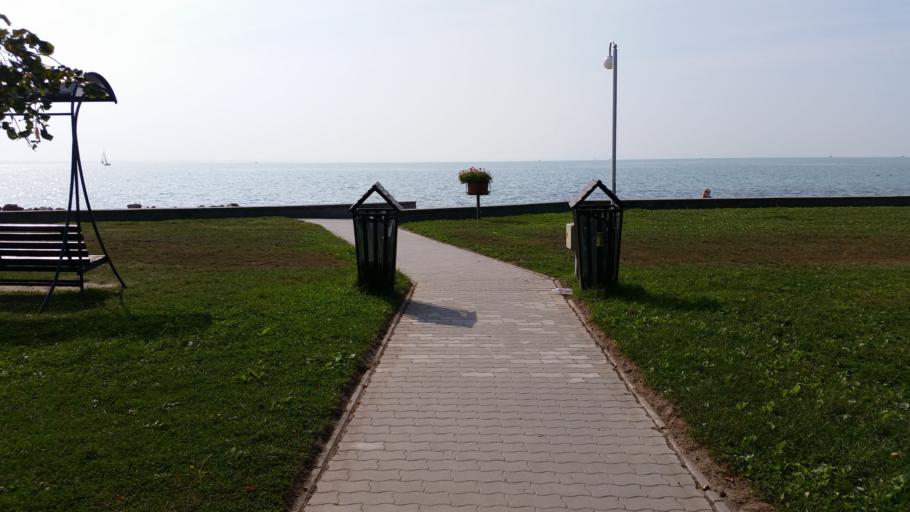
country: HU
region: Veszprem
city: Balatonkenese
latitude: 47.0320
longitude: 18.1144
